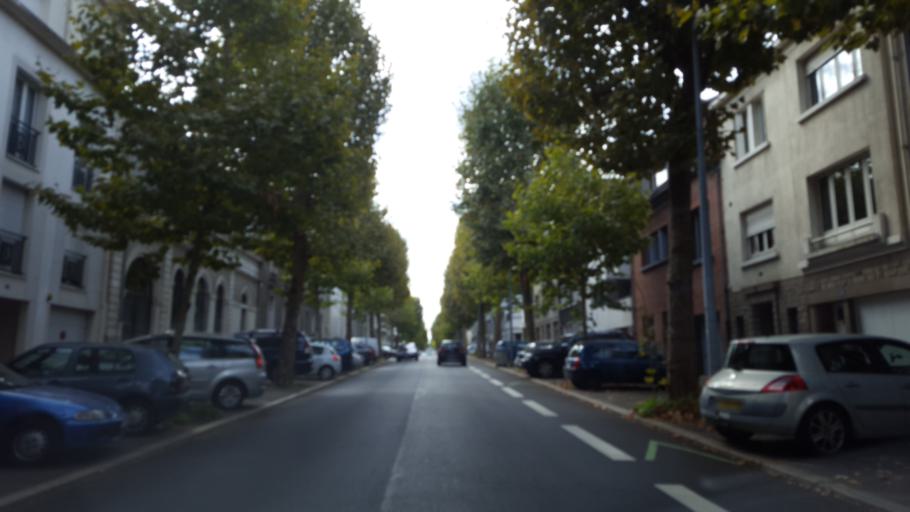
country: FR
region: Pays de la Loire
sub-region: Departement de la Loire-Atlantique
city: Nantes
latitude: 47.2094
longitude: -1.5776
